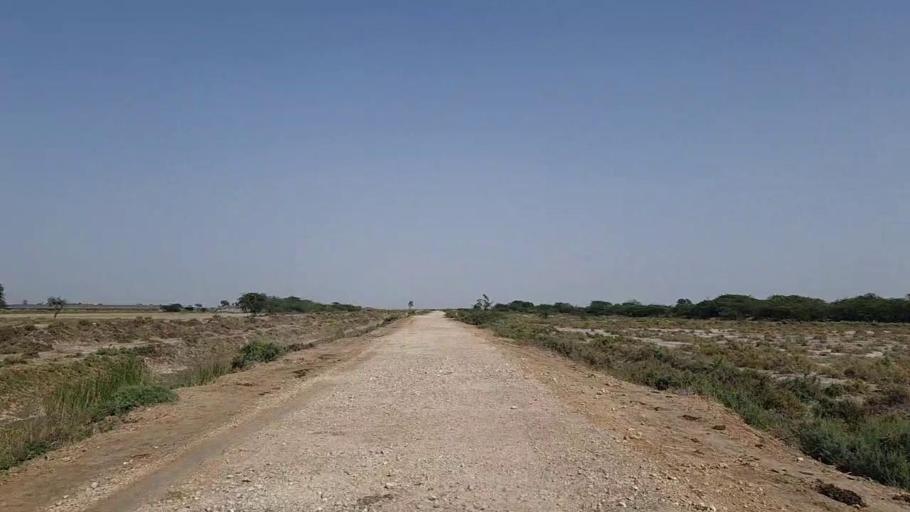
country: PK
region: Sindh
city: Jati
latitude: 24.3608
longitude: 68.2869
